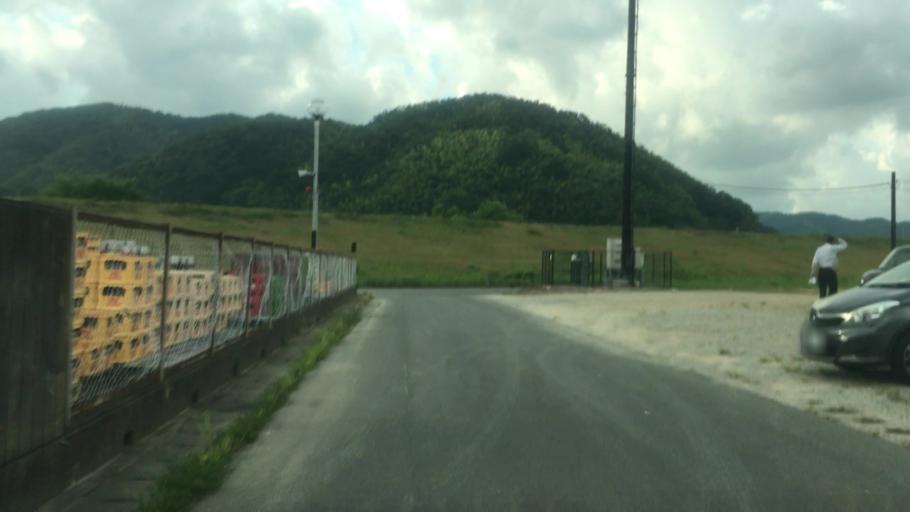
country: JP
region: Hyogo
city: Toyooka
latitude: 35.5625
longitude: 134.8027
